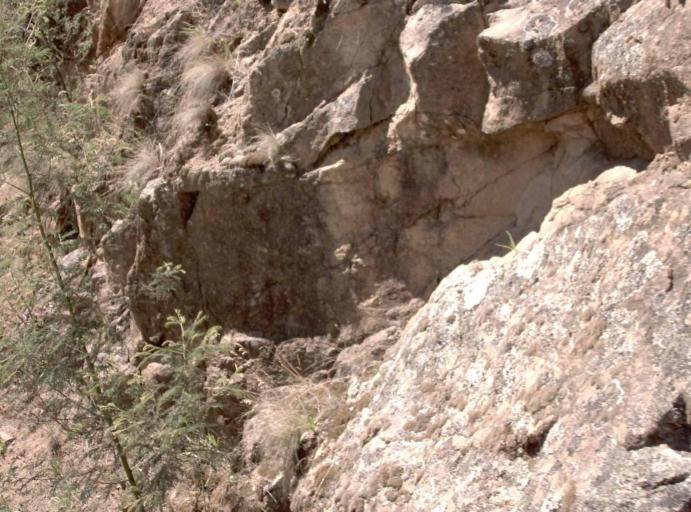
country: AU
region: New South Wales
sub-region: Snowy River
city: Jindabyne
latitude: -37.0446
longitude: 148.5396
